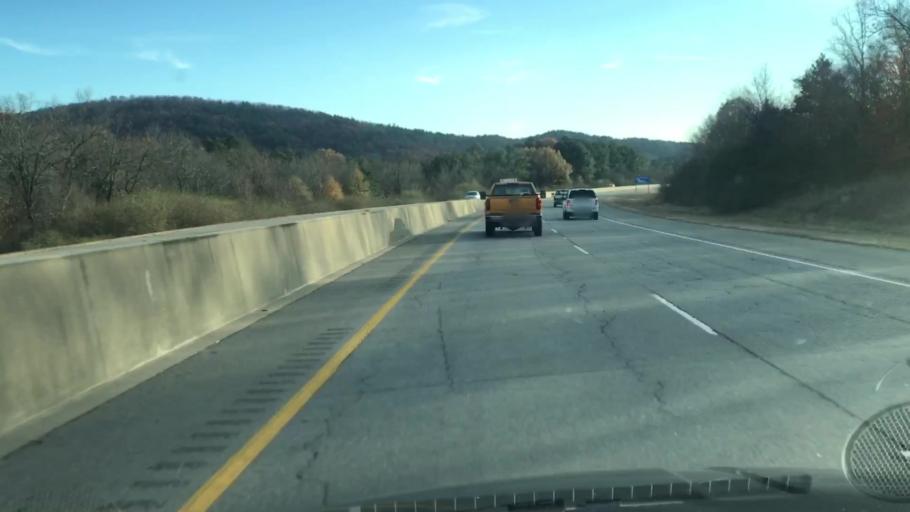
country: US
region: Arkansas
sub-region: Garland County
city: Hot Springs
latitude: 34.4960
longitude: -92.9759
